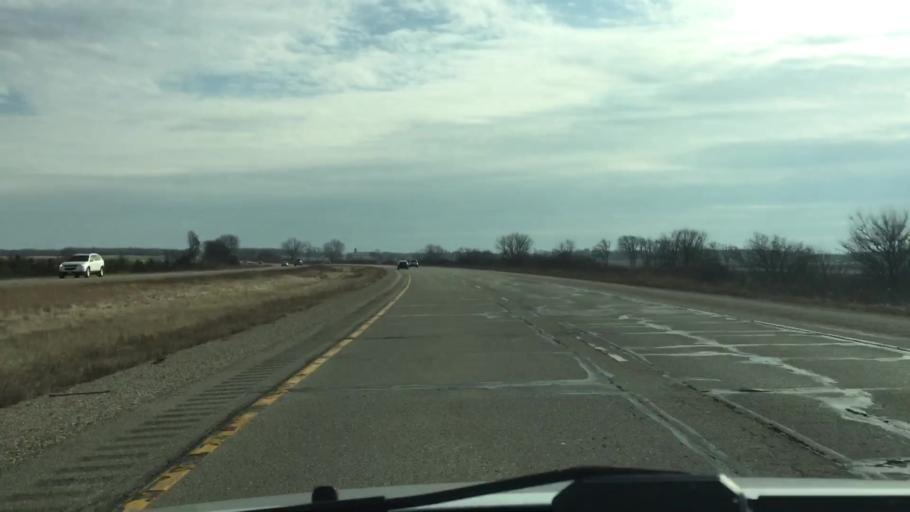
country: US
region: Wisconsin
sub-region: Walworth County
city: Como
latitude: 42.6458
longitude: -88.5018
